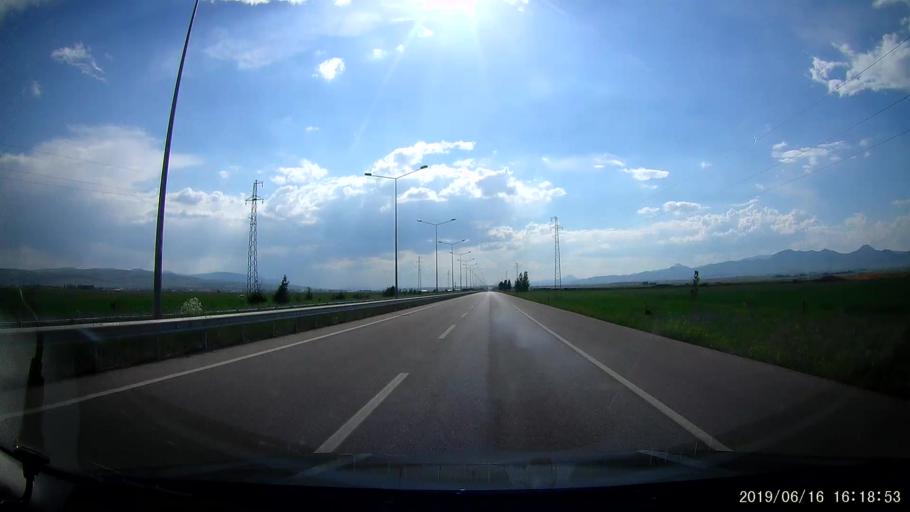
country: TR
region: Erzurum
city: Ilica
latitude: 39.9657
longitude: 41.1555
